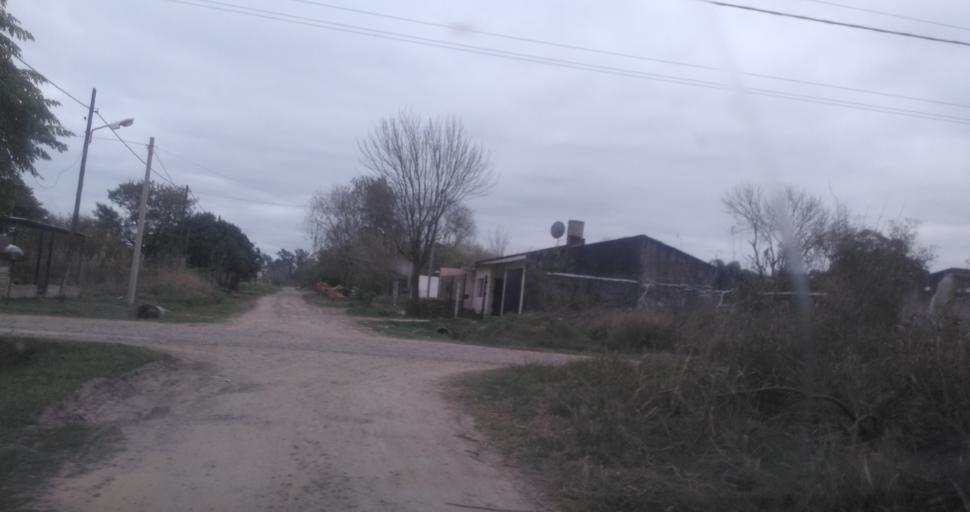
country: AR
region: Chaco
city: Fontana
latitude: -27.4458
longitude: -59.0297
